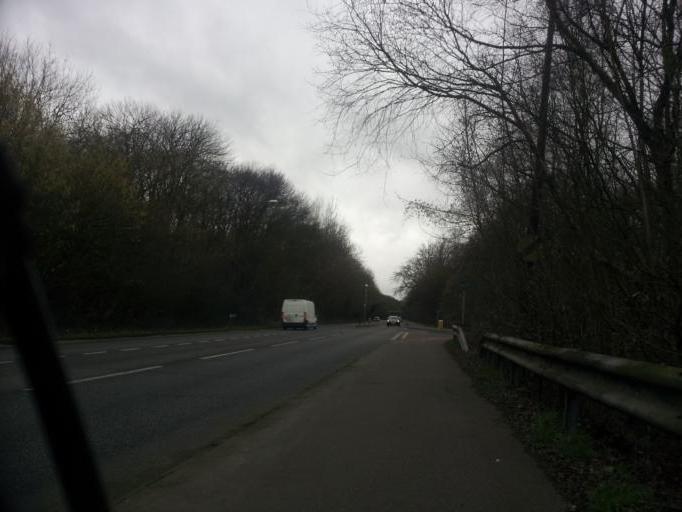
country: GB
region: England
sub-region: Kent
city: Boxley
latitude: 51.3270
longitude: 0.5320
